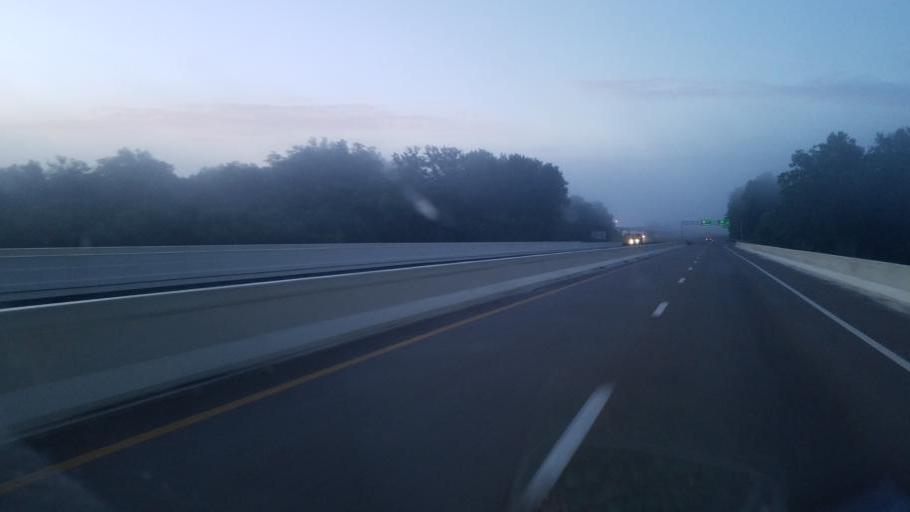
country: US
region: Ohio
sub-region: Ross County
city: Chillicothe
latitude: 39.3067
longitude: -82.9212
